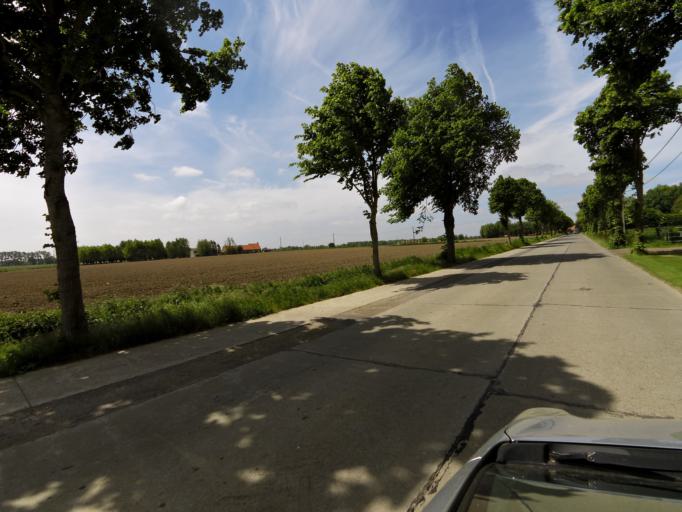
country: BE
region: Flanders
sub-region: Provincie West-Vlaanderen
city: Diksmuide
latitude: 50.9606
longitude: 2.8425
